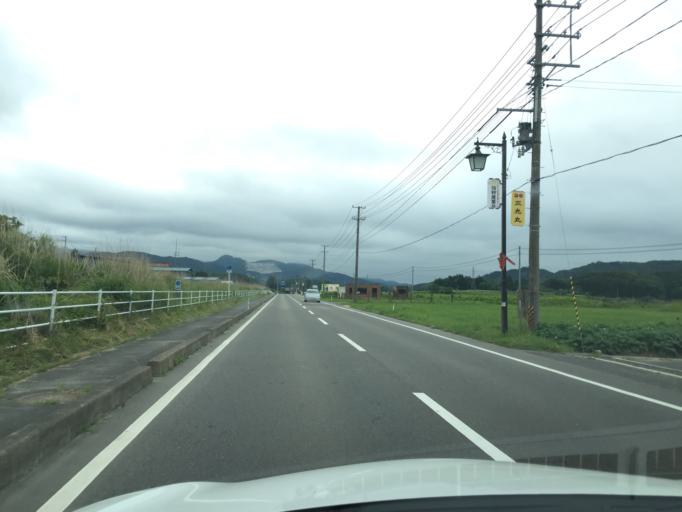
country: JP
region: Fukushima
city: Funehikimachi-funehiki
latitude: 37.4066
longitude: 140.6144
